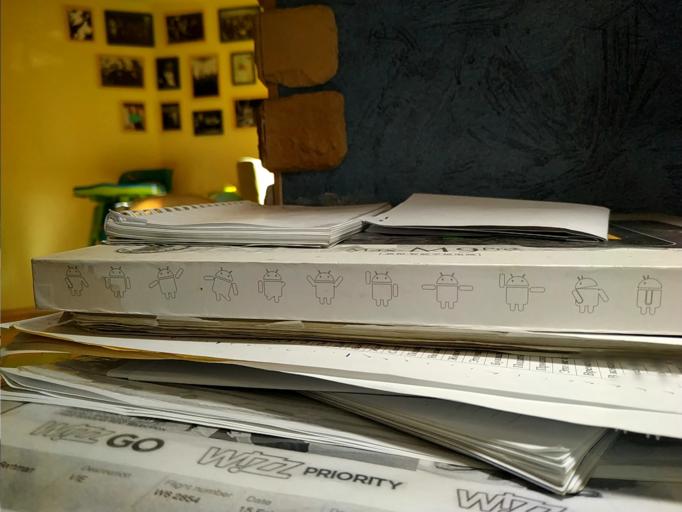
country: RU
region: Novgorod
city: Poddor'ye
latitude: 57.4953
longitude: 30.9526
